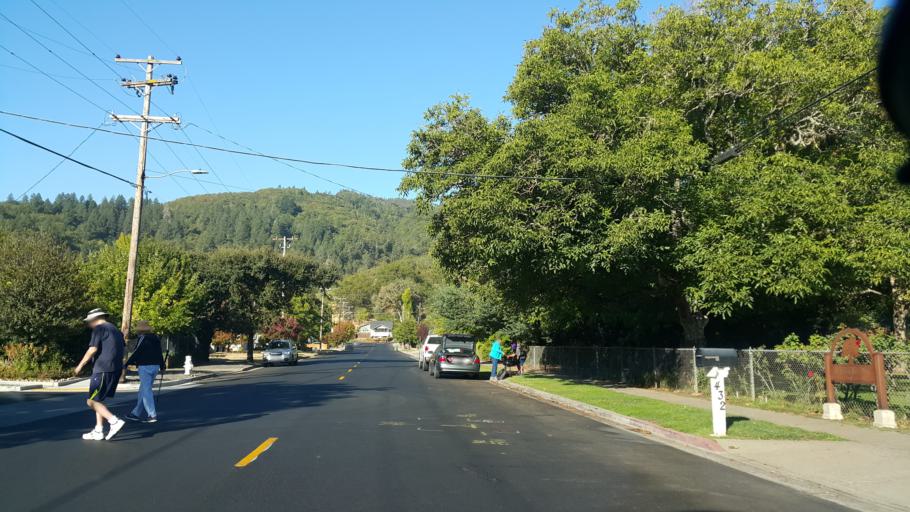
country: US
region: California
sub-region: Mendocino County
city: Ukiah
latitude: 39.1369
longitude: -123.2116
